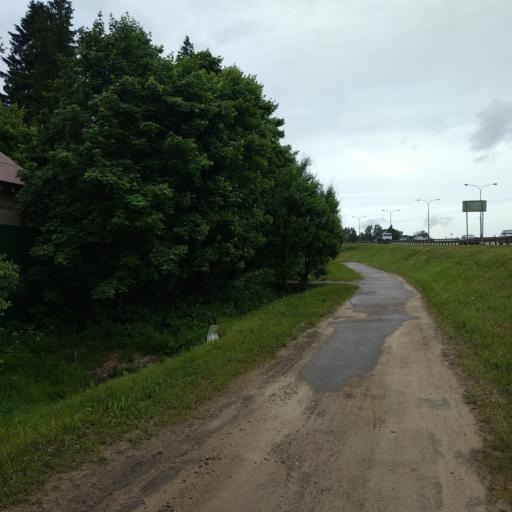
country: RU
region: Moskovskaya
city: Nekrasovskiy
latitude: 56.1213
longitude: 37.5218
